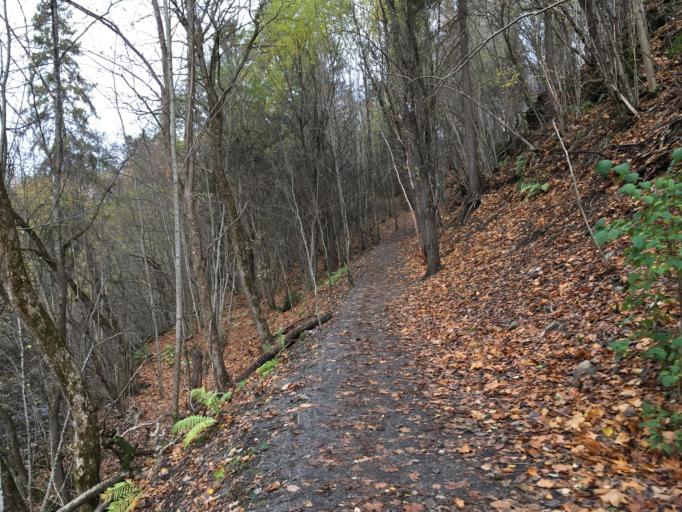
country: NO
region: Akershus
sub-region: Baerum
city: Lysaker
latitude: 59.9345
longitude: 10.6344
